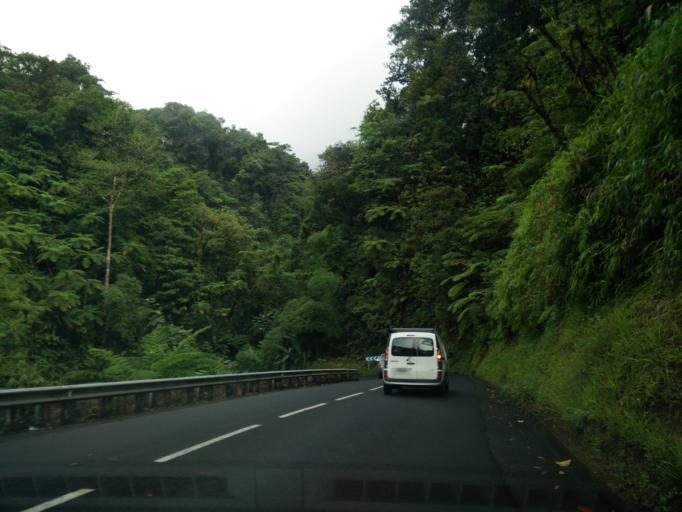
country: MQ
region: Martinique
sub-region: Martinique
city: Saint-Joseph
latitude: 14.7067
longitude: -61.0950
